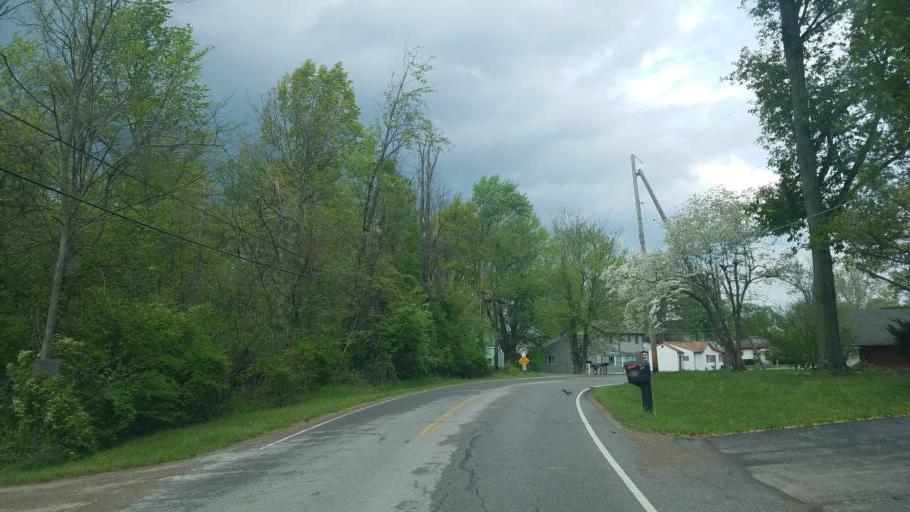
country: US
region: Ohio
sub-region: Fairfield County
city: Fairfield Beach
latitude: 39.9165
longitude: -82.4856
